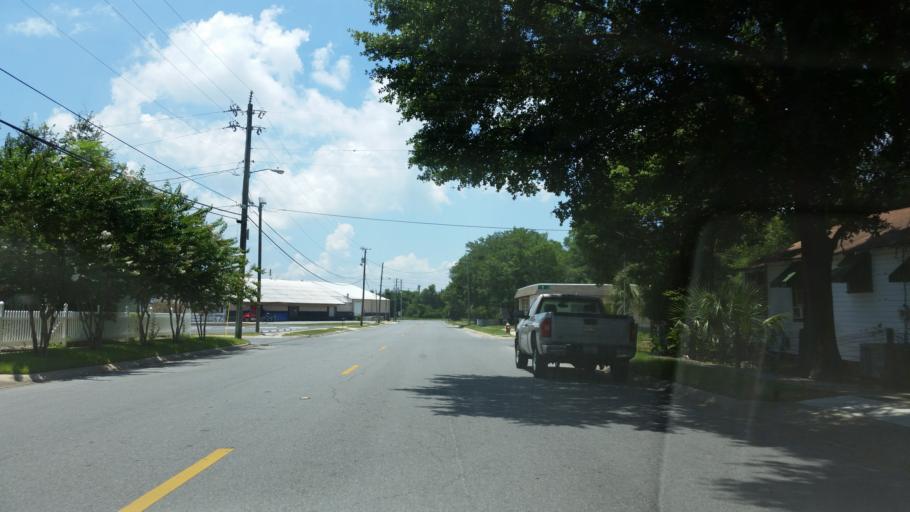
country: US
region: Florida
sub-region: Escambia County
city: Pensacola
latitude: 30.4078
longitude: -87.2393
